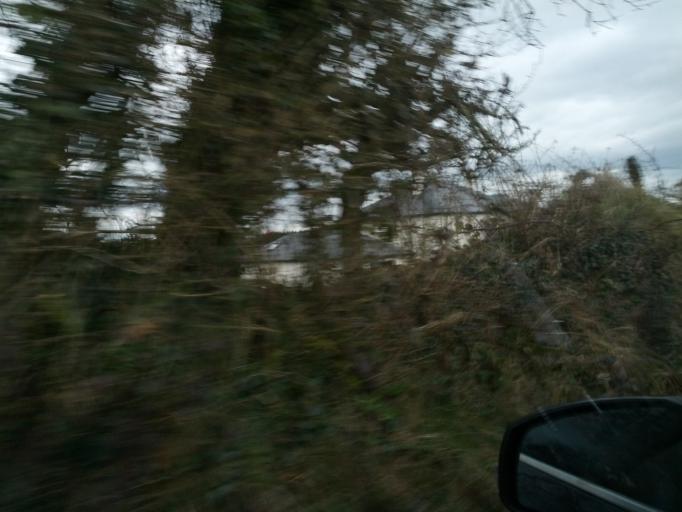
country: IE
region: Connaught
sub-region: County Galway
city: Athenry
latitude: 53.3899
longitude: -8.6432
